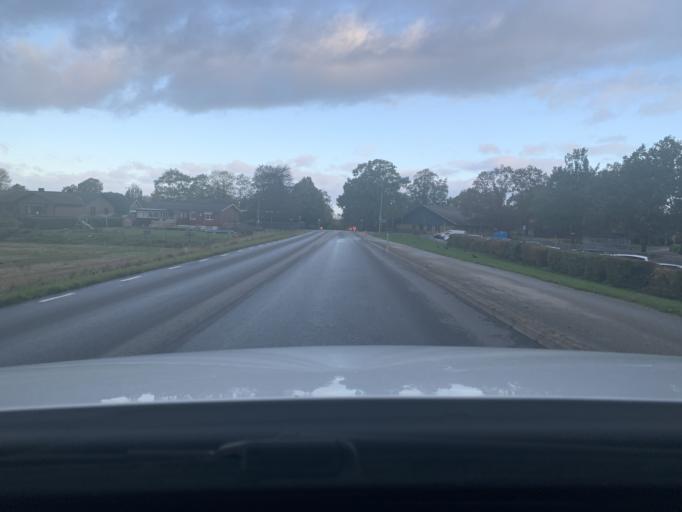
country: SE
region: Skane
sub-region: Horby Kommun
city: Hoerby
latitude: 55.8404
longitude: 13.6577
